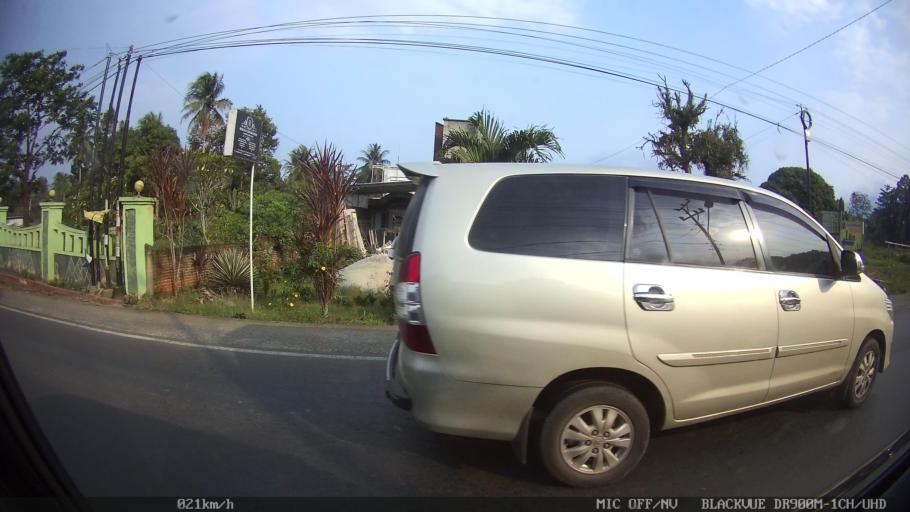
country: ID
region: Lampung
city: Natar
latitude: -5.3649
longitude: 105.1828
